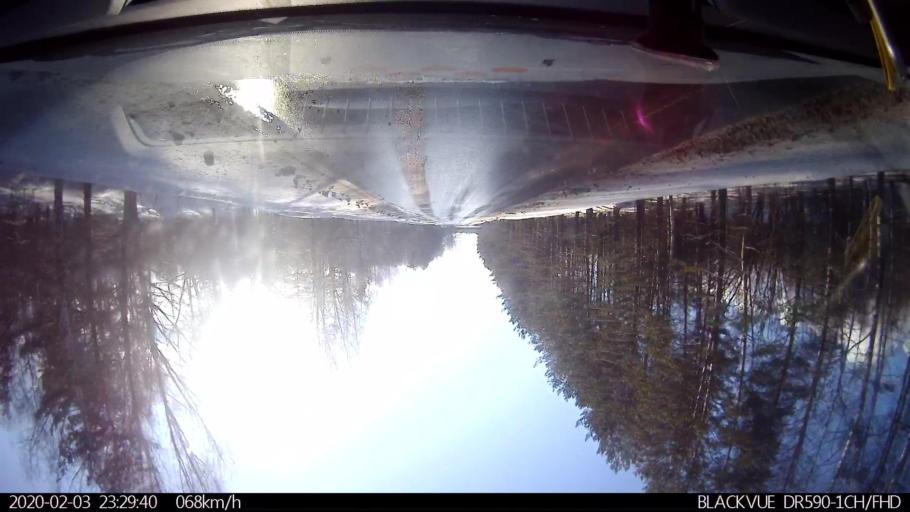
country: RU
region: Nizjnij Novgorod
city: Kstovo
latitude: 55.9602
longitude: 44.2096
